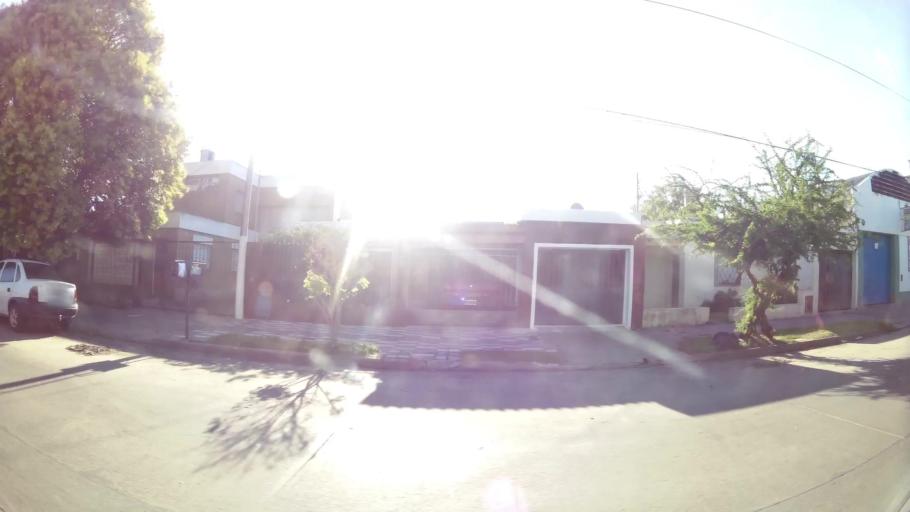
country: AR
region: Cordoba
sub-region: Departamento de Capital
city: Cordoba
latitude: -31.3809
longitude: -64.1893
